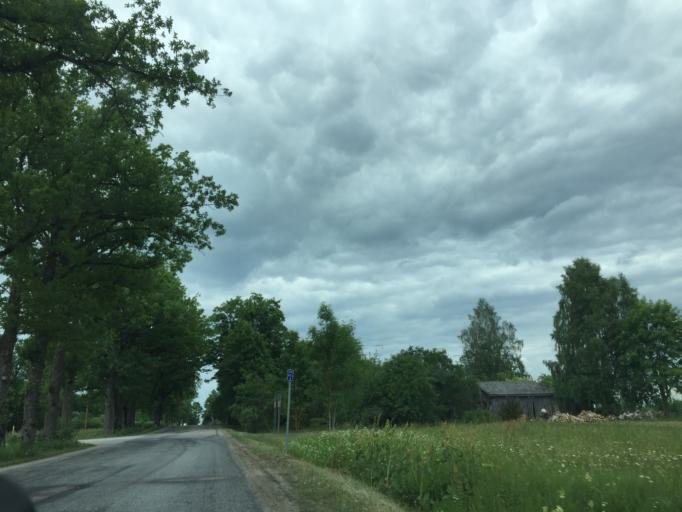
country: LV
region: Skriveri
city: Skriveri
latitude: 56.8328
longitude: 25.1301
